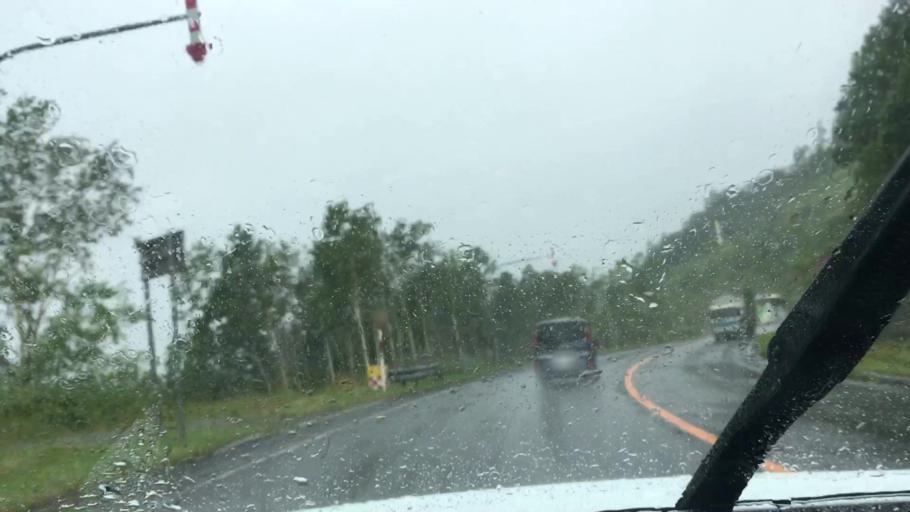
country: JP
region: Hokkaido
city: Sapporo
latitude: 42.8712
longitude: 141.1398
